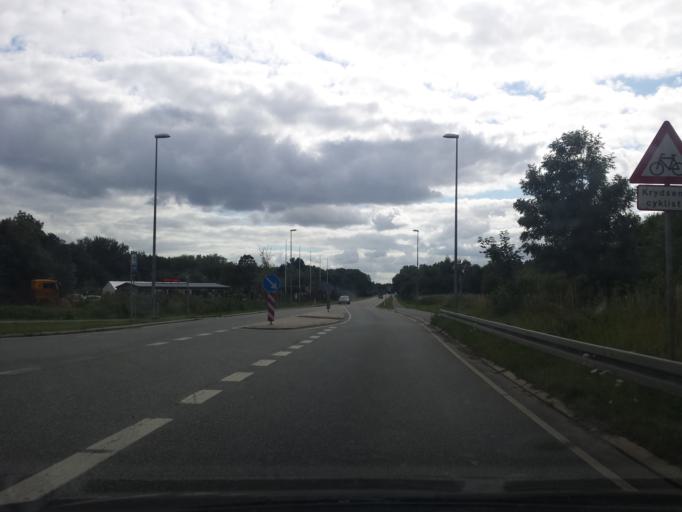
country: DK
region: South Denmark
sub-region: Sonderborg Kommune
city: Augustenborg
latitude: 54.9293
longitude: 9.8429
